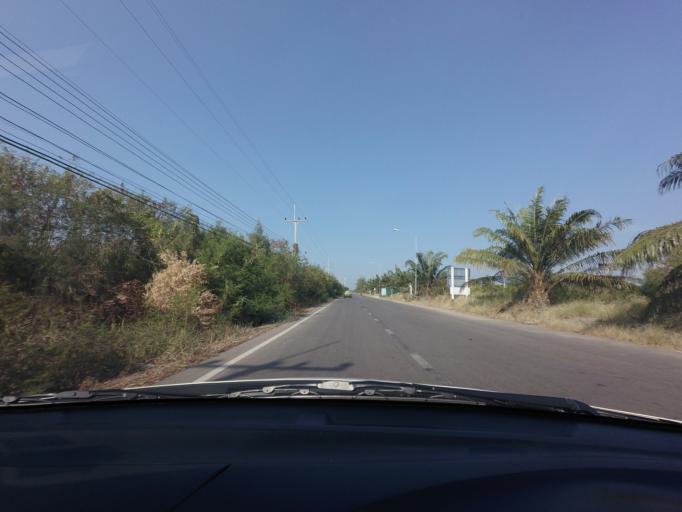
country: TH
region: Samut Sakhon
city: Ban Phaeo
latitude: 13.4981
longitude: 100.0768
